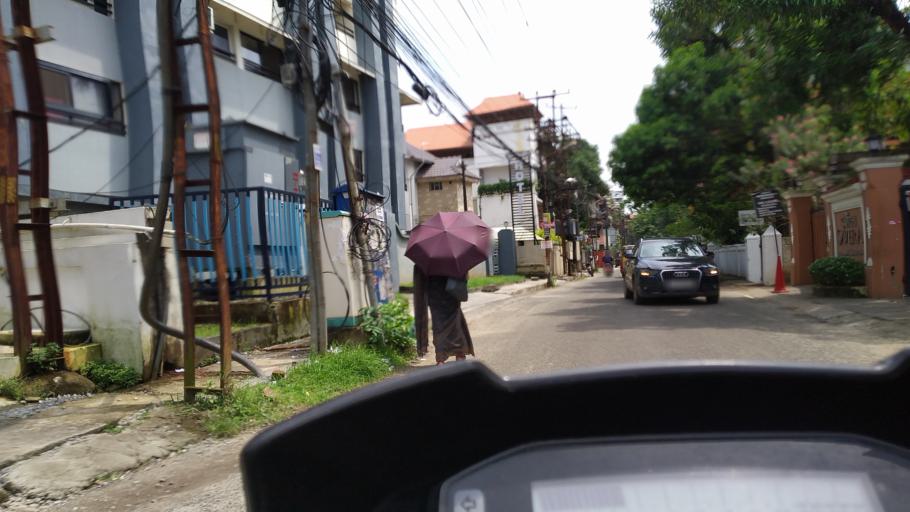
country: IN
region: Kerala
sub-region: Ernakulam
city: Cochin
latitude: 9.9671
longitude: 76.2850
